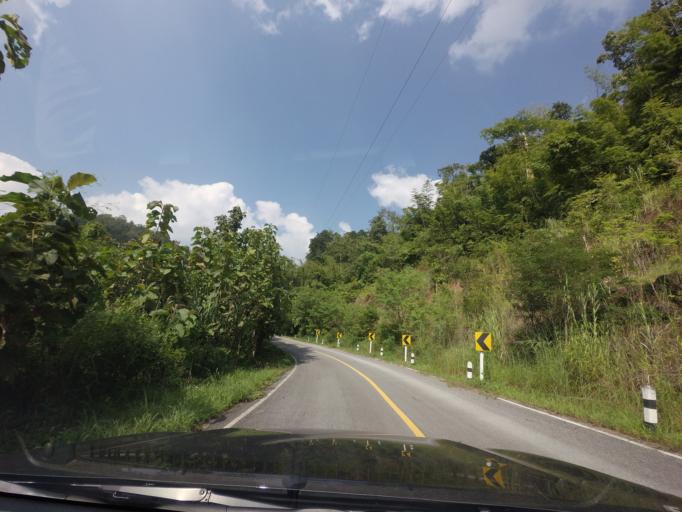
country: TH
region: Uttaradit
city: Ban Khok
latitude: 18.1921
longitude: 101.0524
